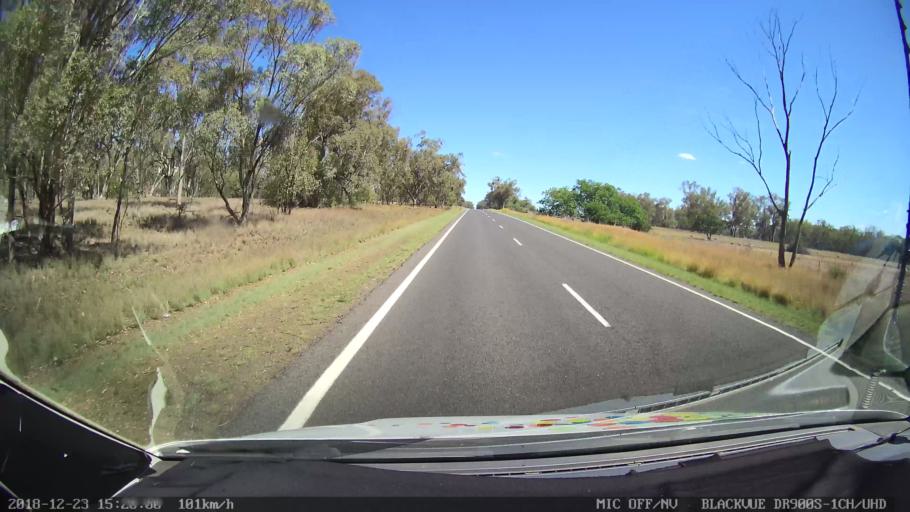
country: AU
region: New South Wales
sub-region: Tamworth Municipality
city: Manilla
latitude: -30.8367
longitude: 150.7867
